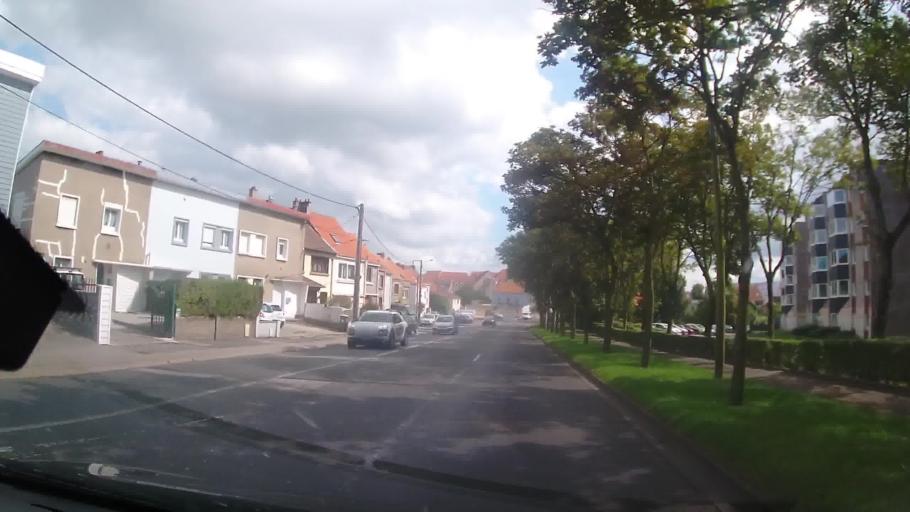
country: FR
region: Nord-Pas-de-Calais
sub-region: Departement du Pas-de-Calais
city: Saint-Martin-Boulogne
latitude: 50.7383
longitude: 1.6202
